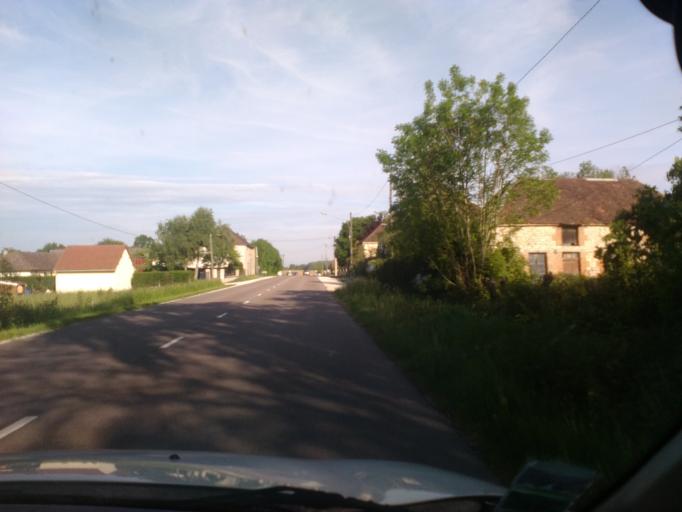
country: FR
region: Champagne-Ardenne
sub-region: Departement de l'Aube
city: Vendeuvre-sur-Barse
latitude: 48.2383
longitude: 4.3831
